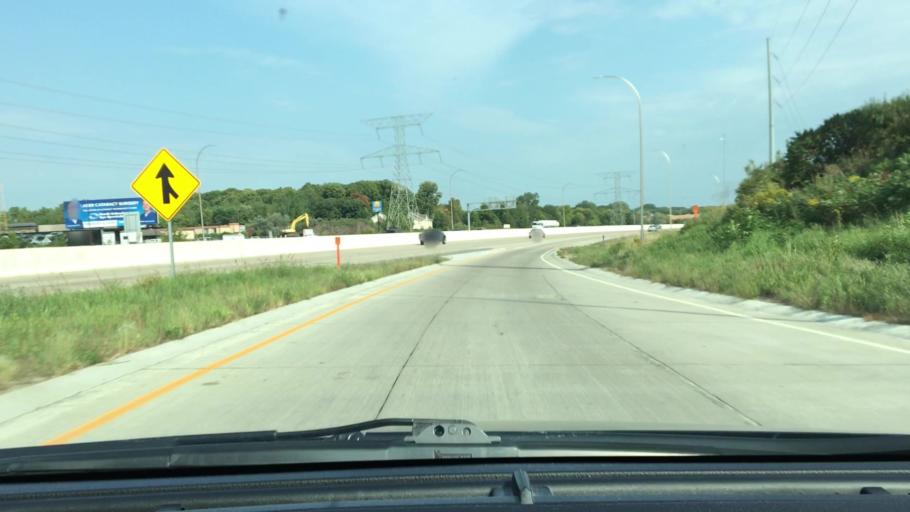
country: US
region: Minnesota
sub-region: Hennepin County
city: Plymouth
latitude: 45.0130
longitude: -93.4569
